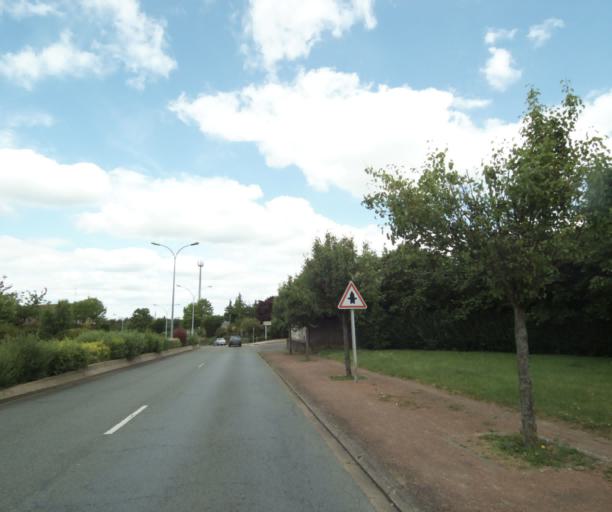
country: FR
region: Centre
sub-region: Departement d'Eure-et-Loir
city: Mainvilliers
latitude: 48.4410
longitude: 1.4515
